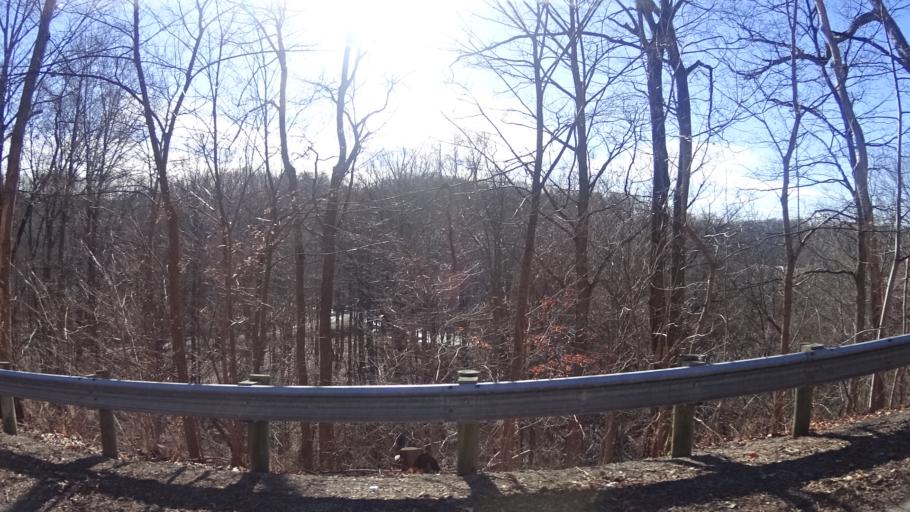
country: US
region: Ohio
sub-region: Lorain County
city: Vermilion
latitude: 41.3613
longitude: -82.3344
